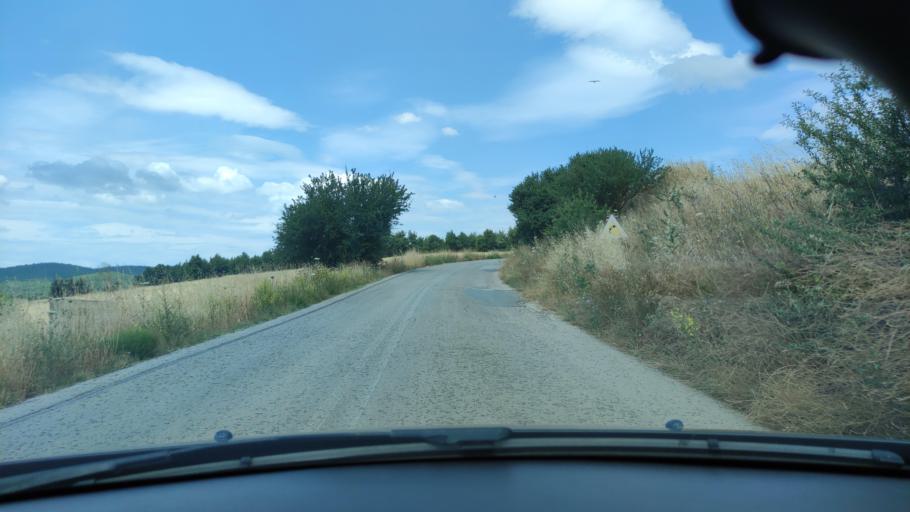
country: GR
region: Central Greece
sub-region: Nomos Evvoias
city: Afration
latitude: 38.5202
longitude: 23.7492
